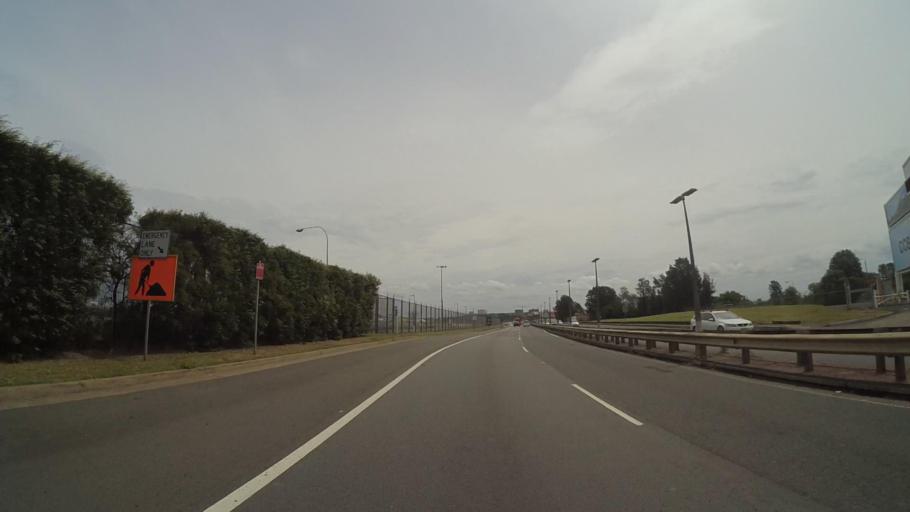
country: AU
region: New South Wales
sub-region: Botany Bay
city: Mascot
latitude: -33.9263
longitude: 151.1766
